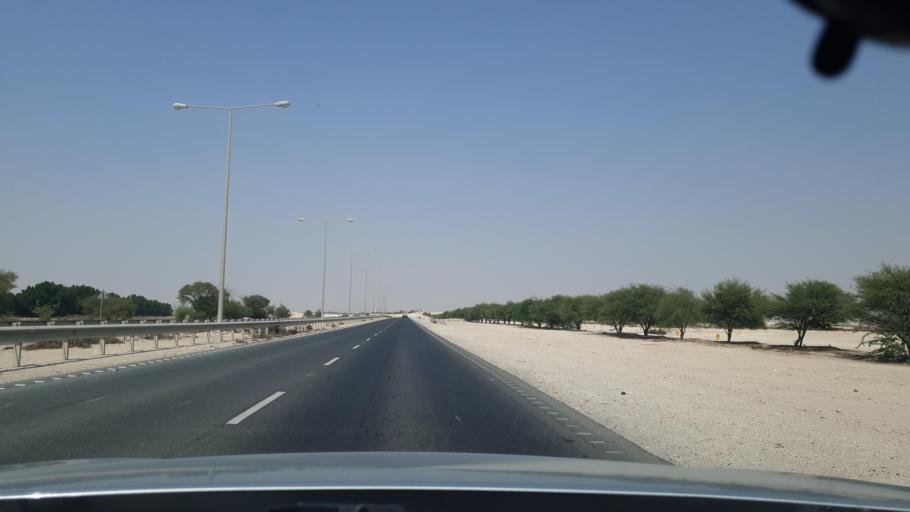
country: QA
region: Al Khawr
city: Al Khawr
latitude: 25.7298
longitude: 51.4951
